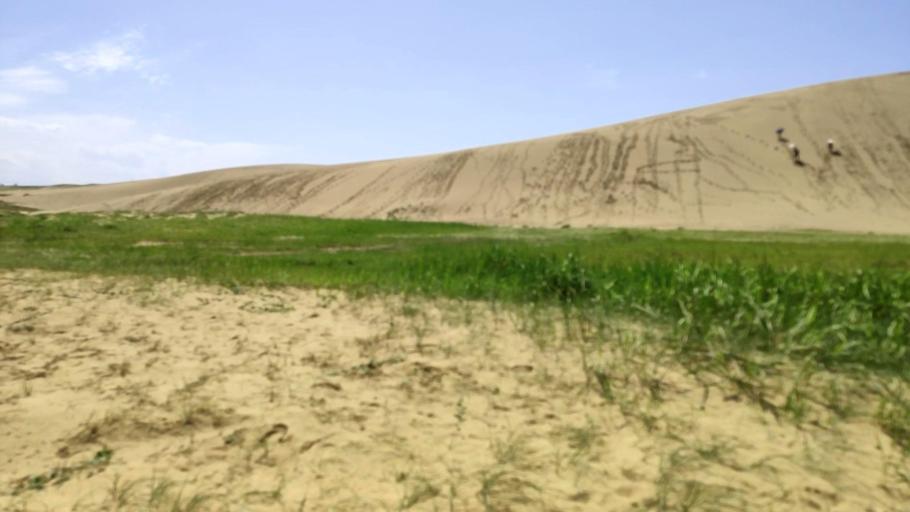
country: JP
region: Tottori
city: Tottori
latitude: 35.5433
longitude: 134.2329
